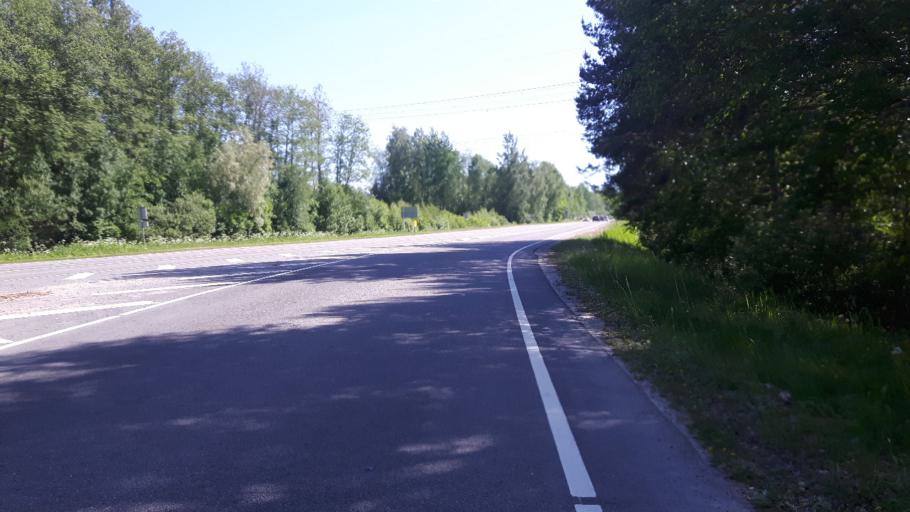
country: EE
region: Paernumaa
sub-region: Paikuse vald
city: Paikuse
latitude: 58.3905
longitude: 24.6414
